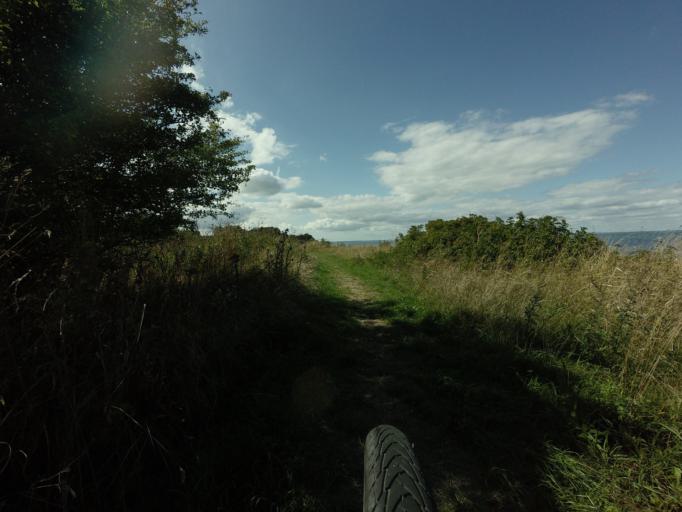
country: DK
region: Zealand
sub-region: Vordingborg Kommune
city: Stege
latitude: 55.0236
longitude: 12.4440
